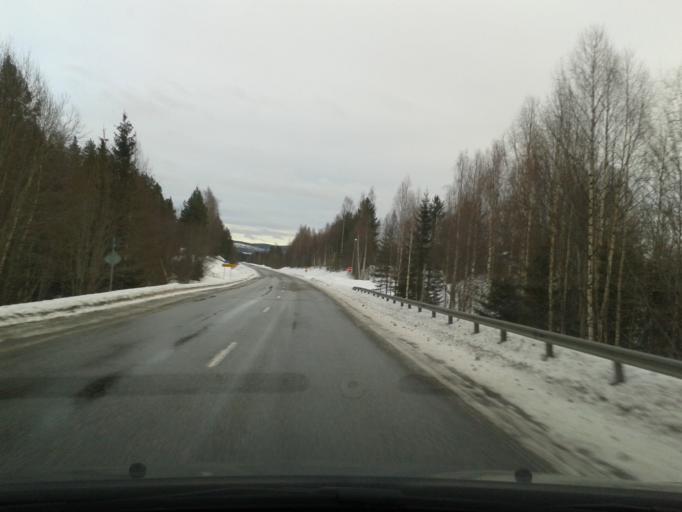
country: SE
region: Vaesternorrland
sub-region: Solleftea Kommun
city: As
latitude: 63.5829
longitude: 16.8232
